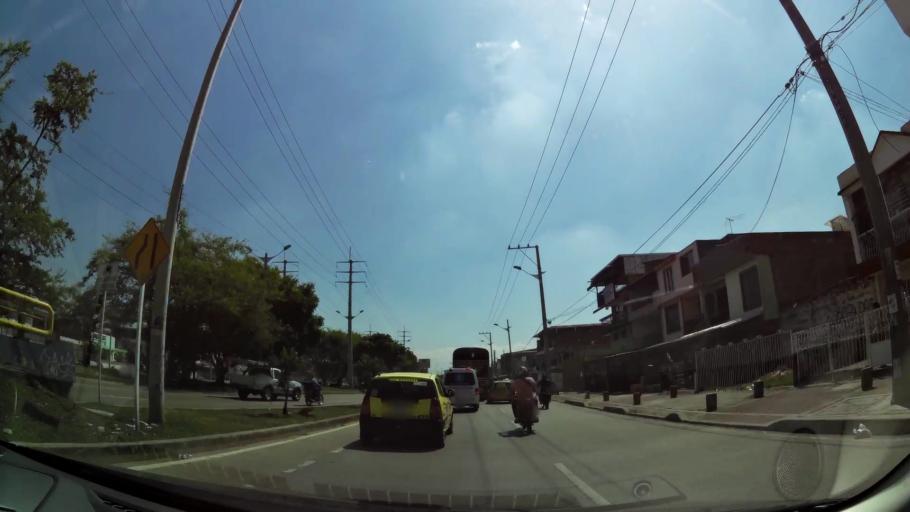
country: CO
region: Valle del Cauca
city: Cali
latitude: 3.4361
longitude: -76.5140
